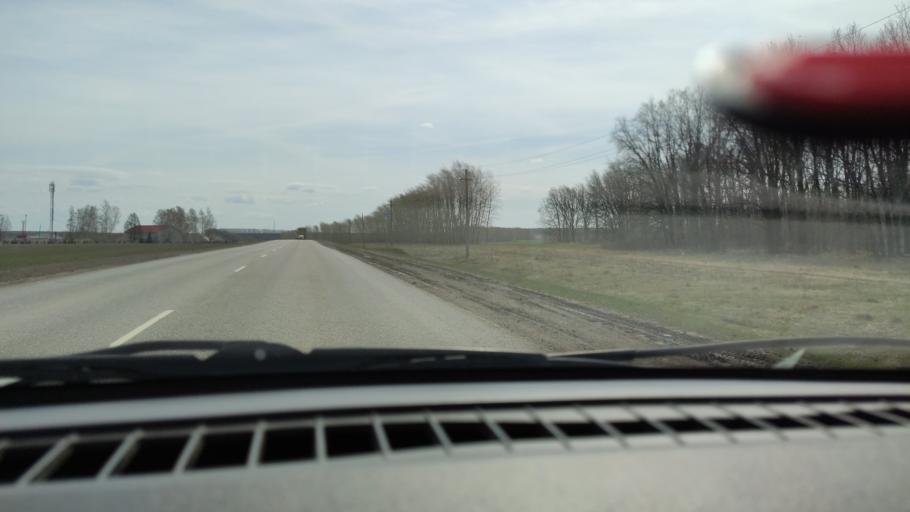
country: RU
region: Bashkortostan
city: Dyurtyuli
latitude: 55.3514
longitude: 54.9155
